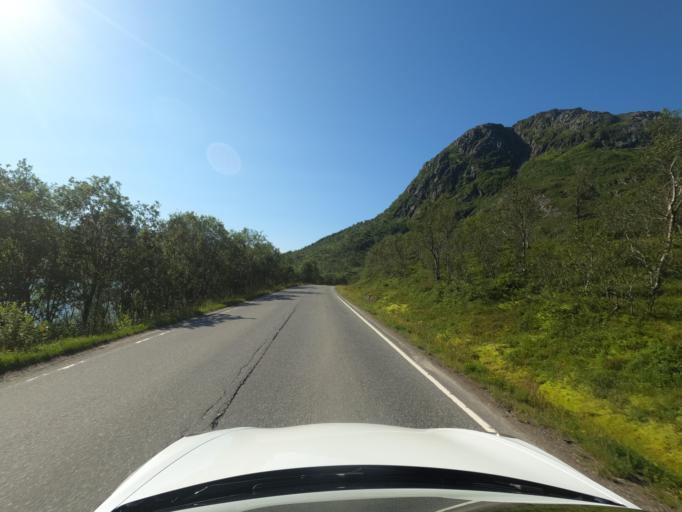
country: NO
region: Nordland
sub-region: Lodingen
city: Lodingen
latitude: 68.5594
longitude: 15.7506
